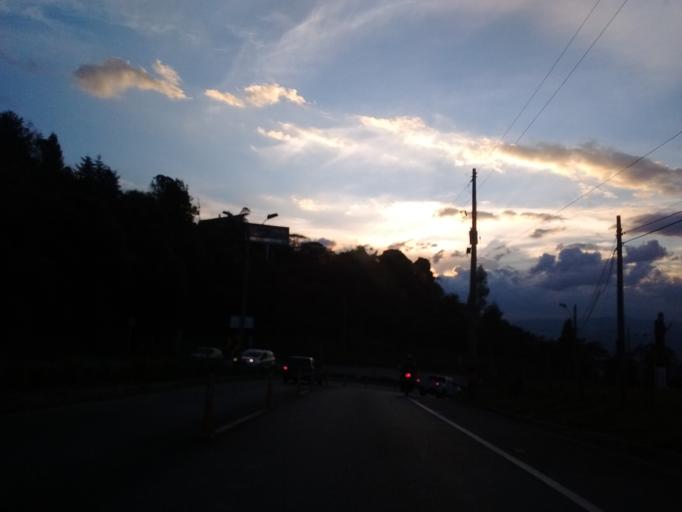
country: CO
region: Antioquia
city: Envigado
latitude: 6.1521
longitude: -75.5461
